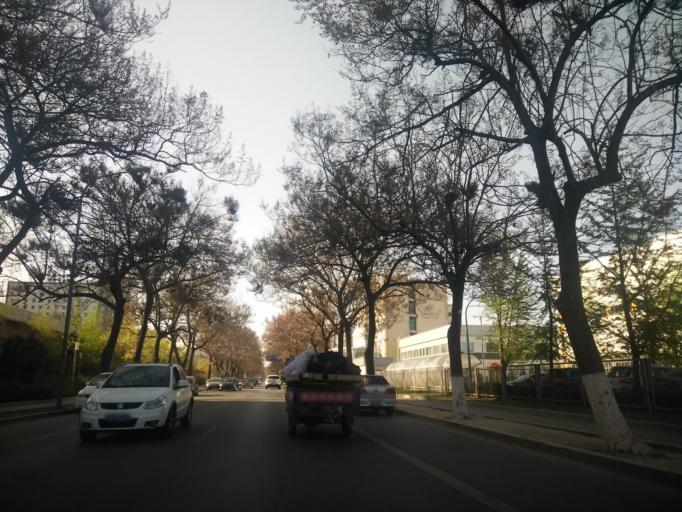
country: CN
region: Beijing
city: Jiugong
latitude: 39.7955
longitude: 116.5050
